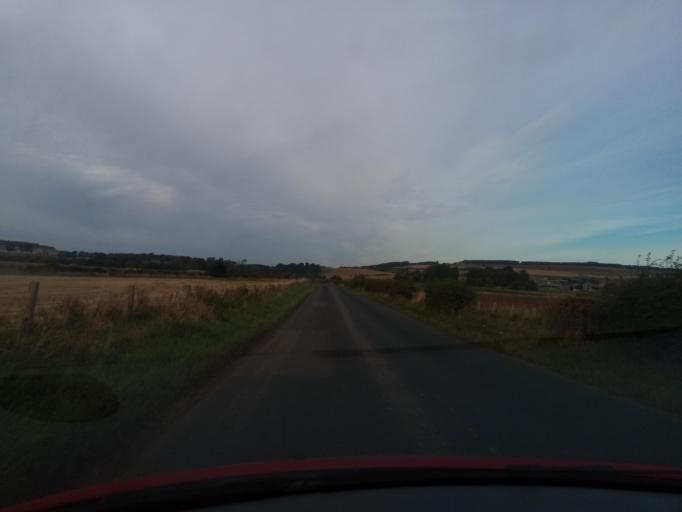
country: GB
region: Scotland
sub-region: The Scottish Borders
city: Kelso
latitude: 55.5195
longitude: -2.3929
